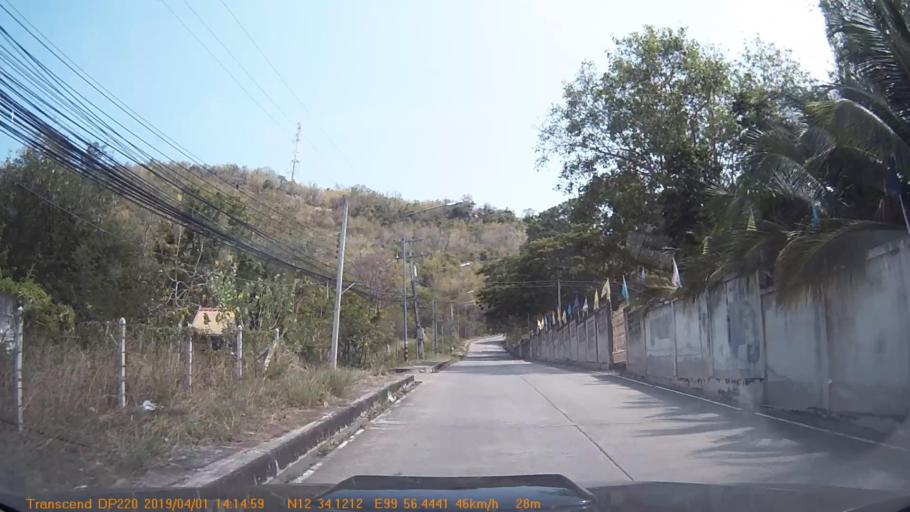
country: TH
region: Prachuap Khiri Khan
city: Hua Hin
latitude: 12.5686
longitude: 99.9408
